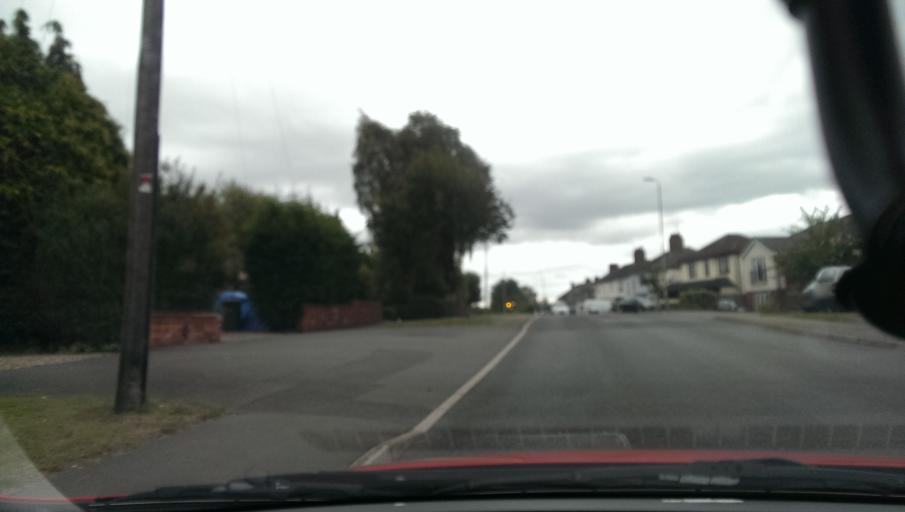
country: GB
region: England
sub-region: Leicestershire
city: Wigston Magna
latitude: 52.5809
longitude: -1.0996
